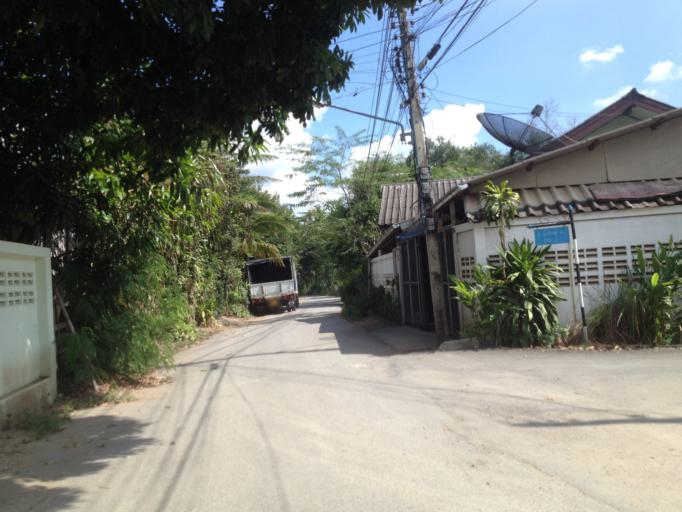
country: TH
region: Chiang Mai
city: Hang Dong
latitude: 18.7334
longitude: 98.9232
